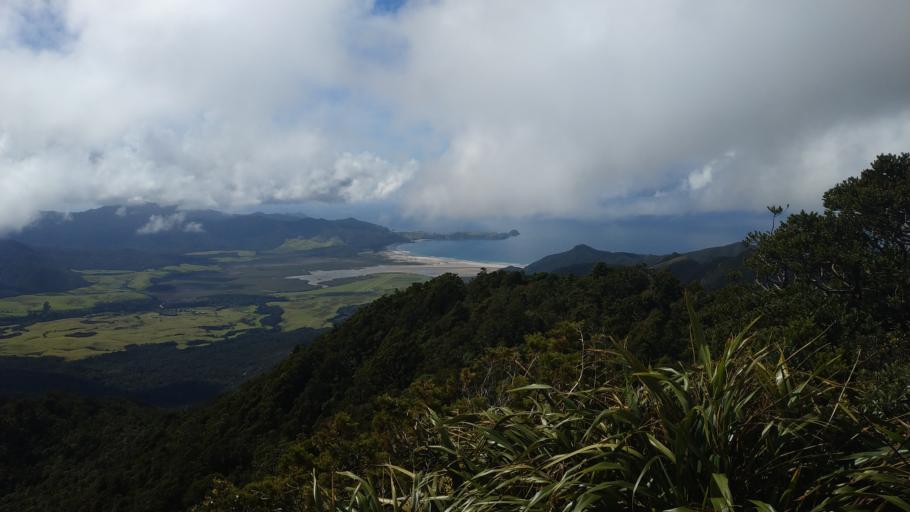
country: NZ
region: Waikato
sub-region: Thames-Coromandel District
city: Coromandel
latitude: -36.1860
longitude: 175.4128
